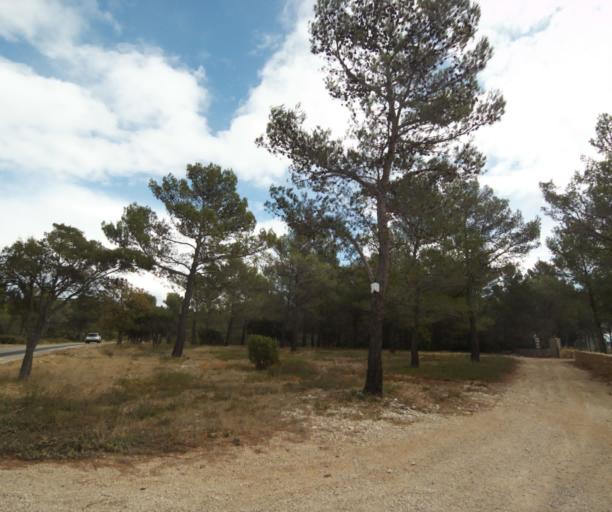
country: FR
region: Provence-Alpes-Cote d'Azur
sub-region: Departement des Bouches-du-Rhone
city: Cuges-les-Pins
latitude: 43.2418
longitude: 5.7069
